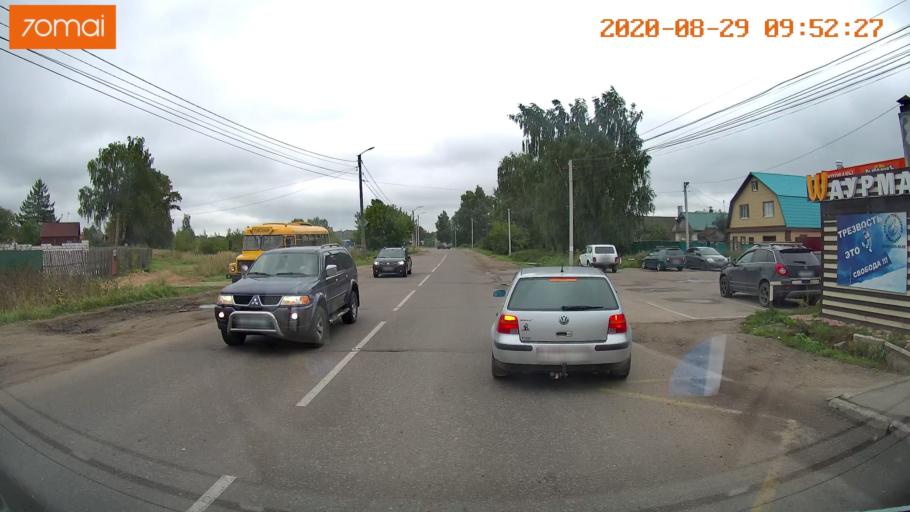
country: RU
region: Ivanovo
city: Kineshma
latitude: 57.4238
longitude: 42.2091
